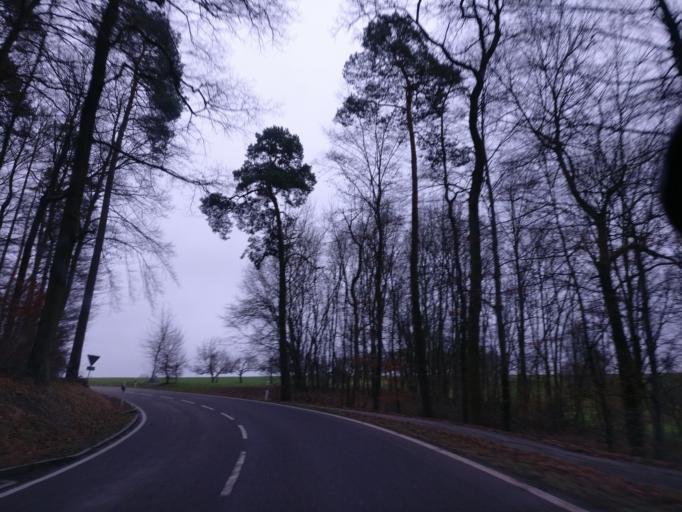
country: DE
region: Baden-Wuerttemberg
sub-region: Regierungsbezirk Stuttgart
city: Rudersberg
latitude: 48.8491
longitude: 9.4930
